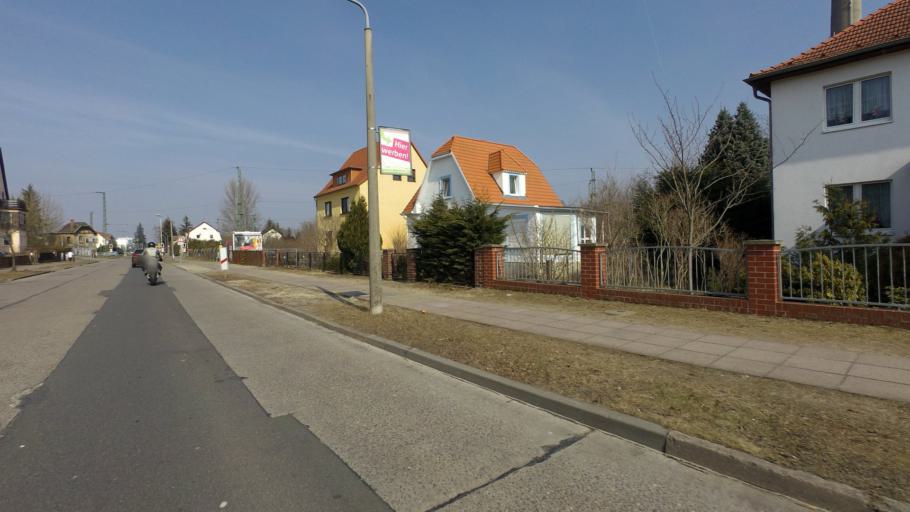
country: DE
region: Brandenburg
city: Werder
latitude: 52.3934
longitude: 12.9221
